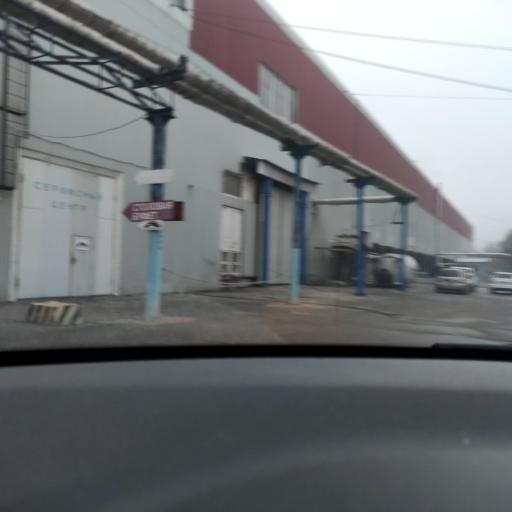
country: RU
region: Samara
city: Samara
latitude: 53.1920
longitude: 50.2581
